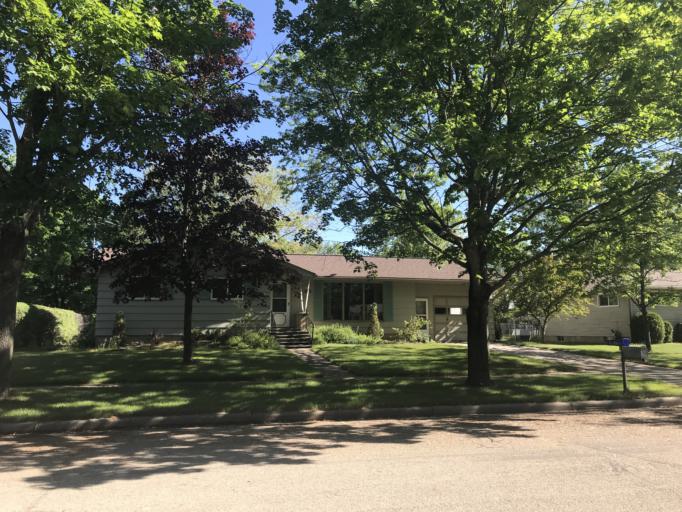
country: US
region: Wisconsin
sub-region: Marinette County
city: Peshtigo
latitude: 45.0510
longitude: -87.7597
